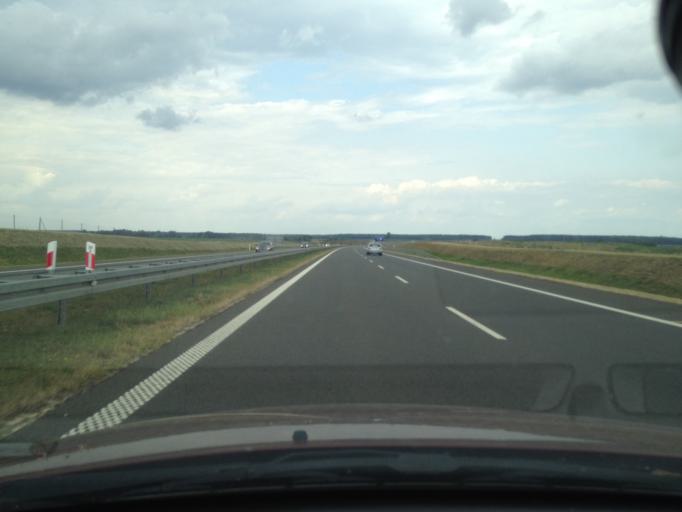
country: PL
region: West Pomeranian Voivodeship
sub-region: Powiat pyrzycki
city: Bielice
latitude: 53.1300
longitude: 14.7301
